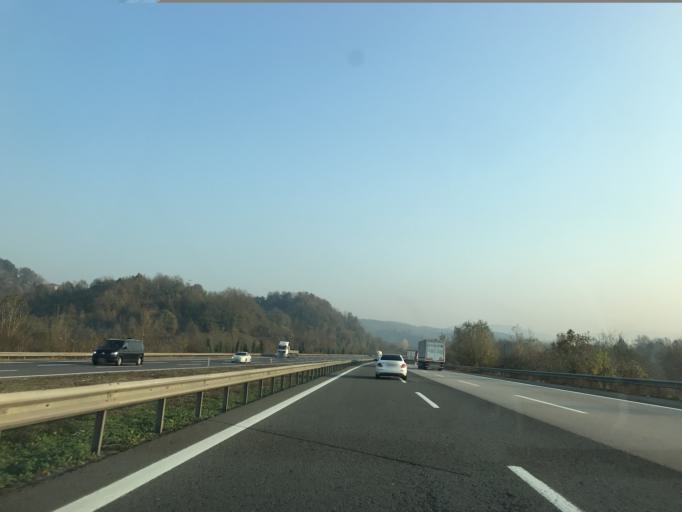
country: TR
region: Sakarya
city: Hendek
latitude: 40.7736
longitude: 30.7841
